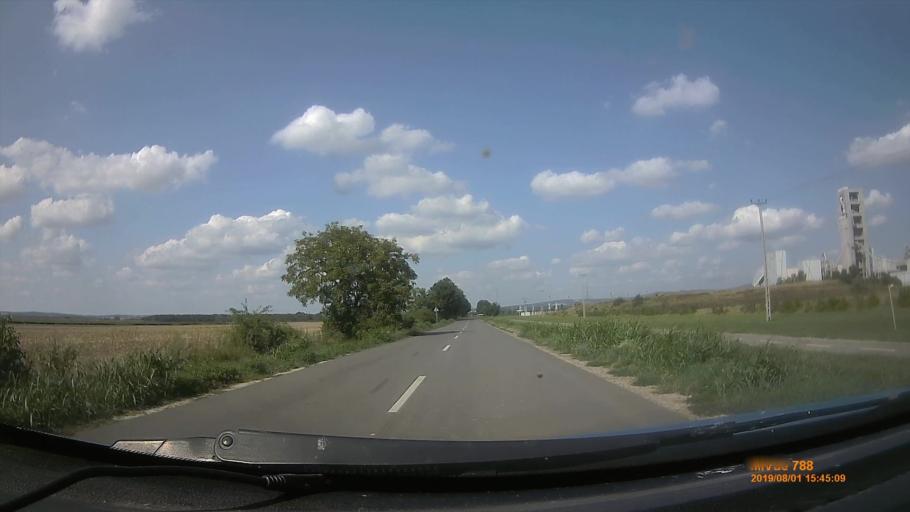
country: HU
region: Baranya
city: Szentlorinc
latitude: 46.0133
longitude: 17.9756
